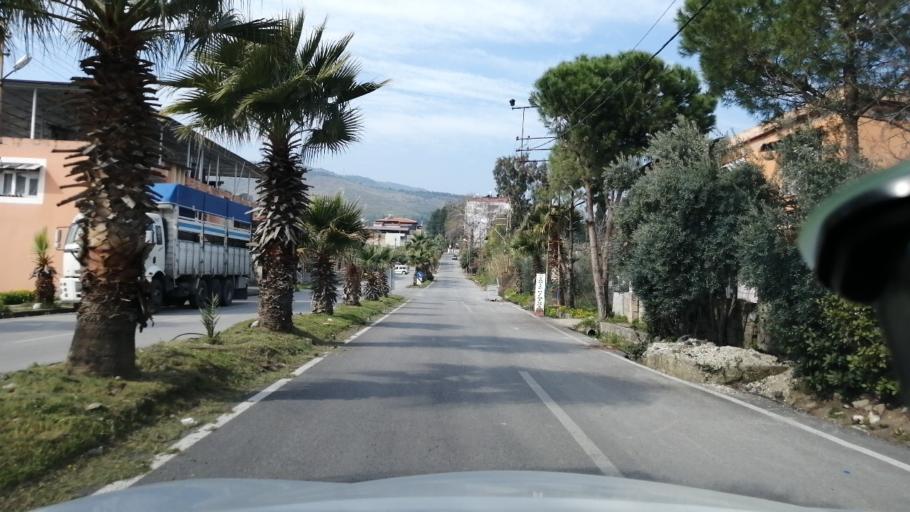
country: TR
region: Hatay
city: Serinyol
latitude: 36.3528
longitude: 36.2099
